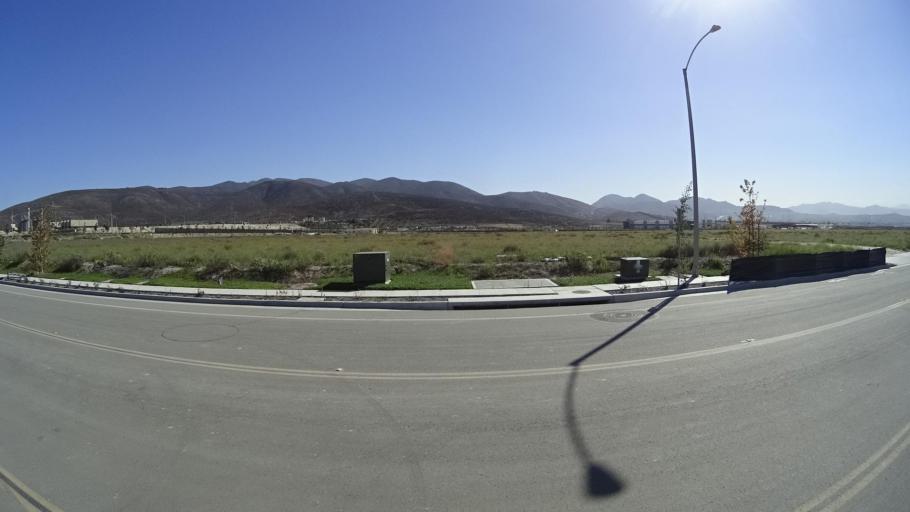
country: MX
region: Baja California
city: Tijuana
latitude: 32.5661
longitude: -116.9192
